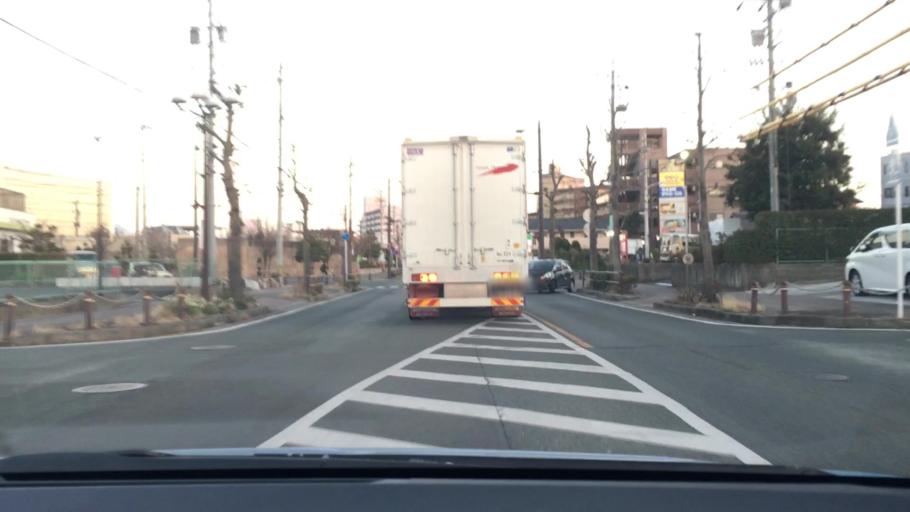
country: JP
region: Aichi
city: Tahara
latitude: 34.6654
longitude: 137.2666
